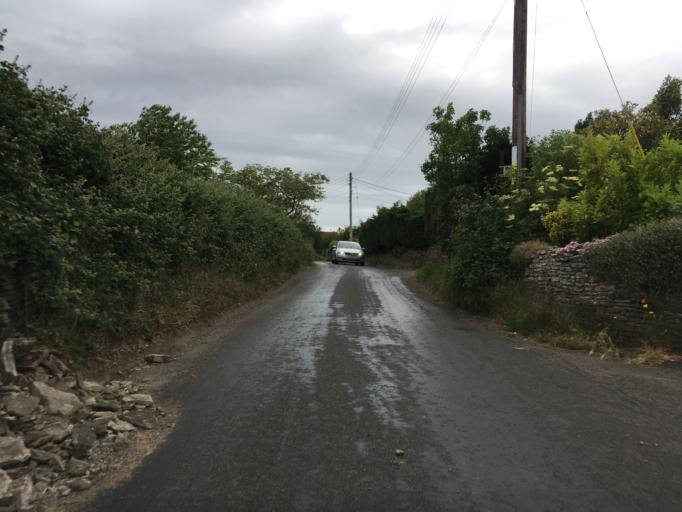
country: GB
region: England
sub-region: North Somerset
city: Brockley
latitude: 51.4163
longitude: -2.7921
